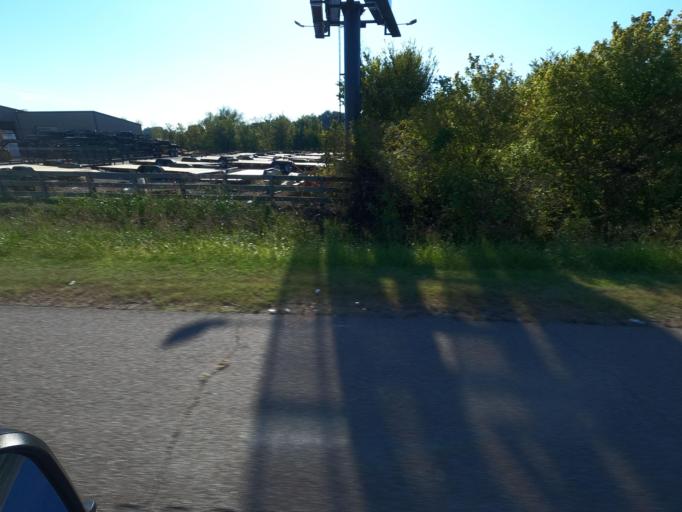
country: US
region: Tennessee
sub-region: Crockett County
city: Alamo
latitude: 35.8839
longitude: -89.2289
